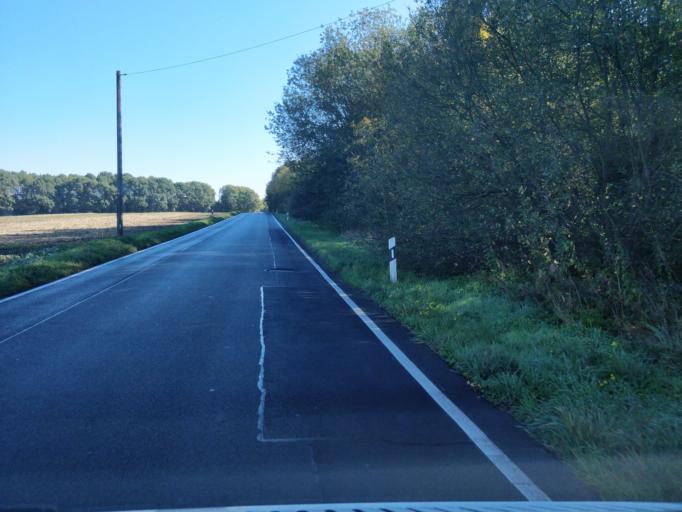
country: DE
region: North Rhine-Westphalia
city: Monheim am Rhein
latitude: 51.0422
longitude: 6.8864
